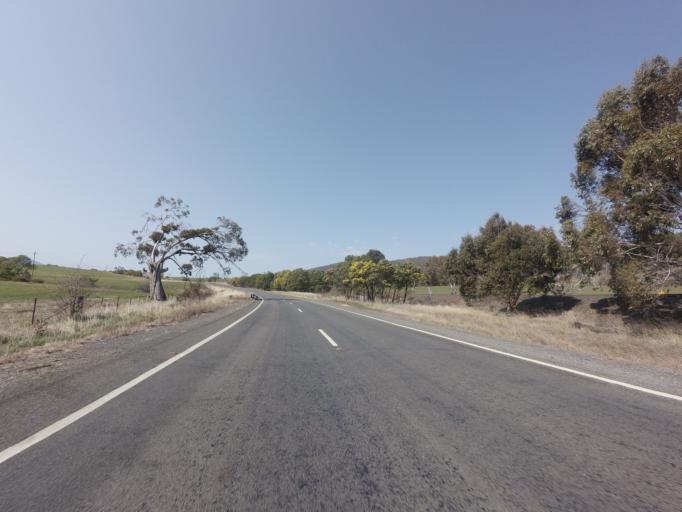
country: AU
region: Tasmania
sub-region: Northern Midlands
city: Evandale
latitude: -41.8121
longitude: 147.6074
